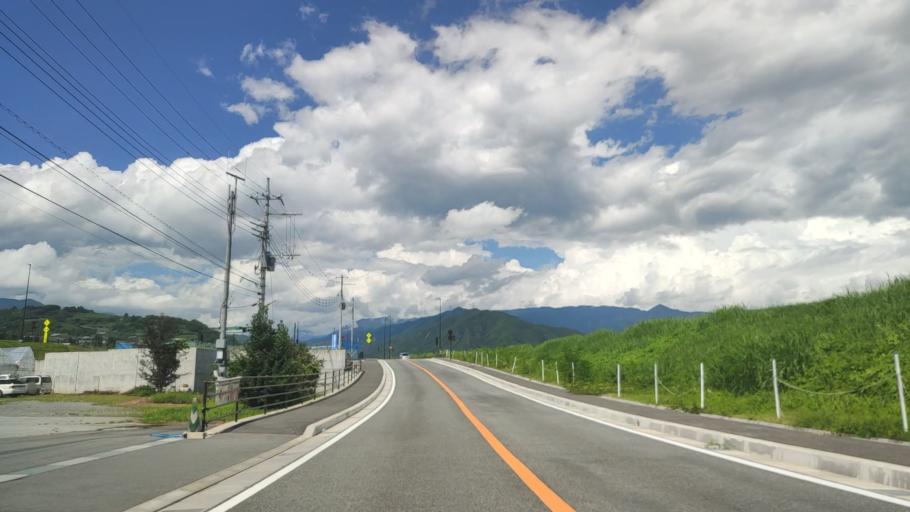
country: JP
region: Yamanashi
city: Enzan
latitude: 35.7088
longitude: 138.6983
